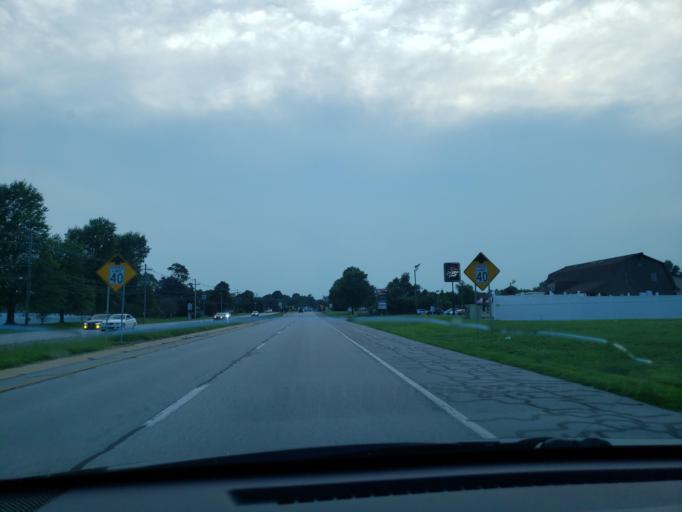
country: US
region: Delaware
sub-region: Kent County
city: Highland Acres
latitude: 39.1182
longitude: -75.5095
